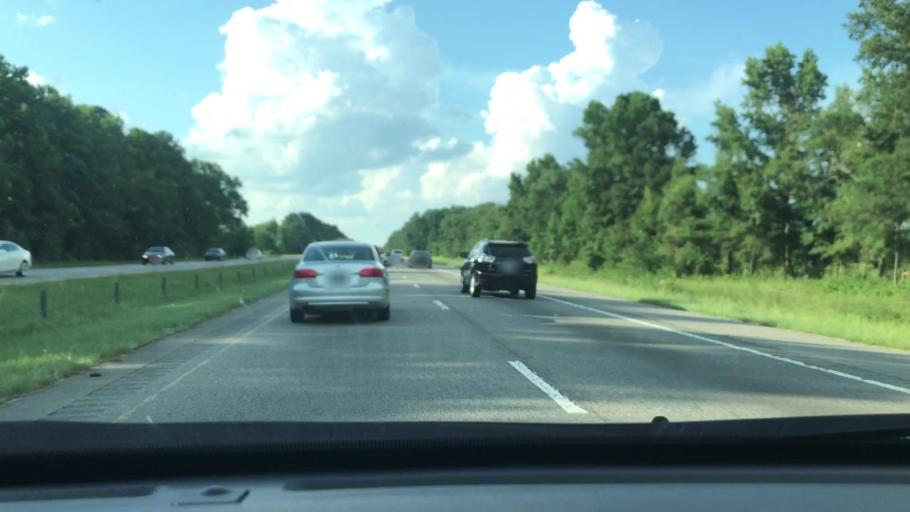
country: US
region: North Carolina
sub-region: Robeson County
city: Saint Pauls
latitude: 34.7444
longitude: -78.9971
